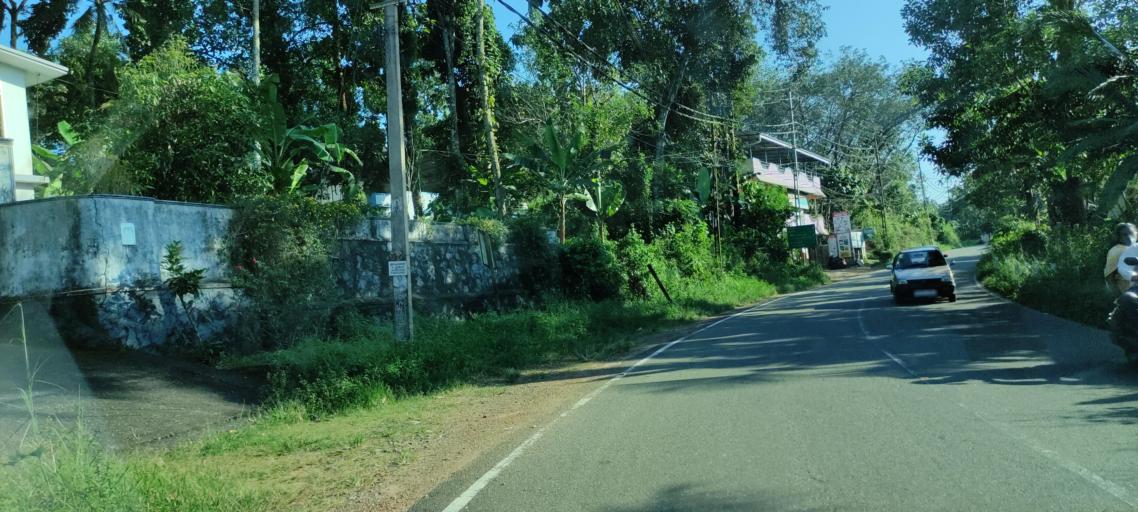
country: IN
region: Kerala
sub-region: Pattanamtitta
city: Adur
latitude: 9.1723
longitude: 76.7417
